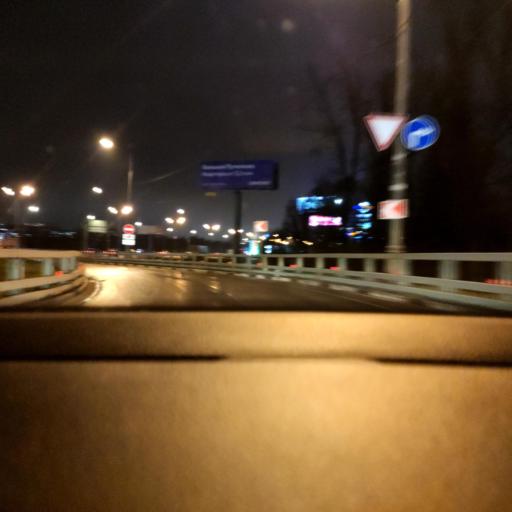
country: RU
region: Moscow
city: Khimki
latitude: 55.8639
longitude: 37.4002
